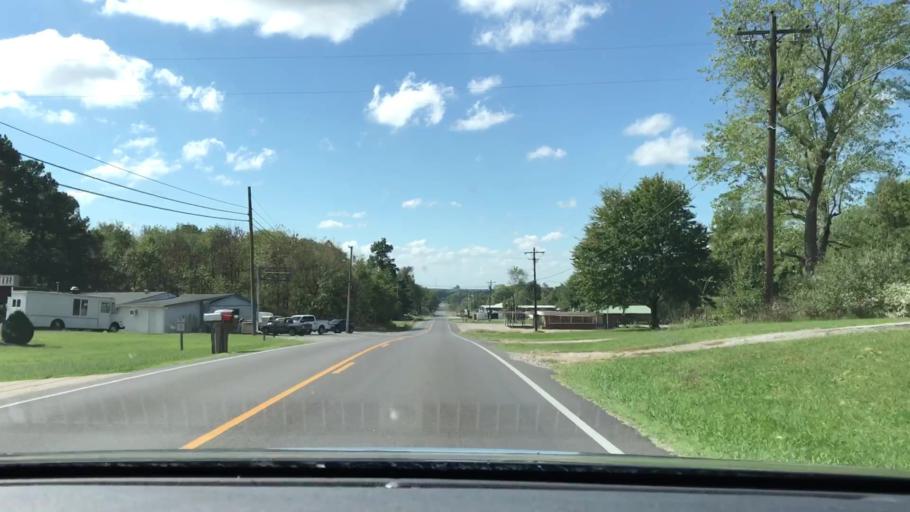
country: US
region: Kentucky
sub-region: Graves County
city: Mayfield
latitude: 36.7567
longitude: -88.6045
